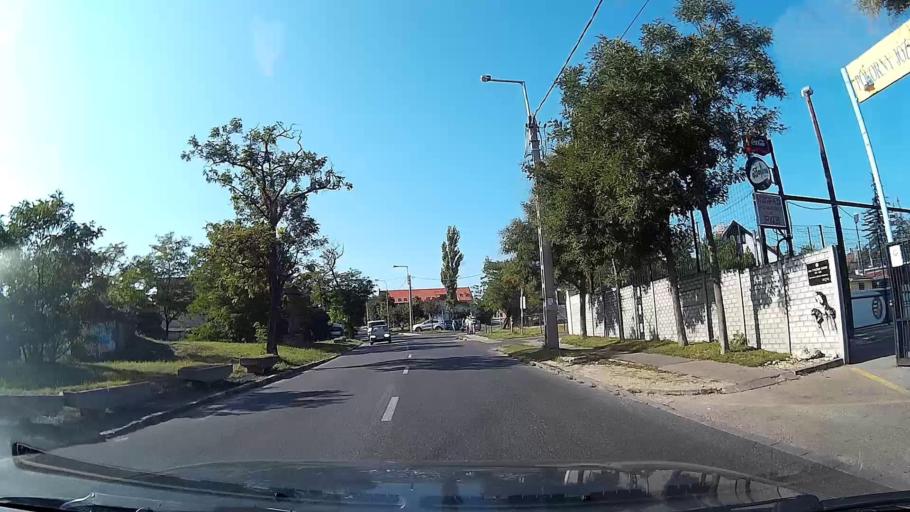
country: HU
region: Budapest
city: Budapest XXII. keruelet
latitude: 47.4150
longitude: 19.0155
